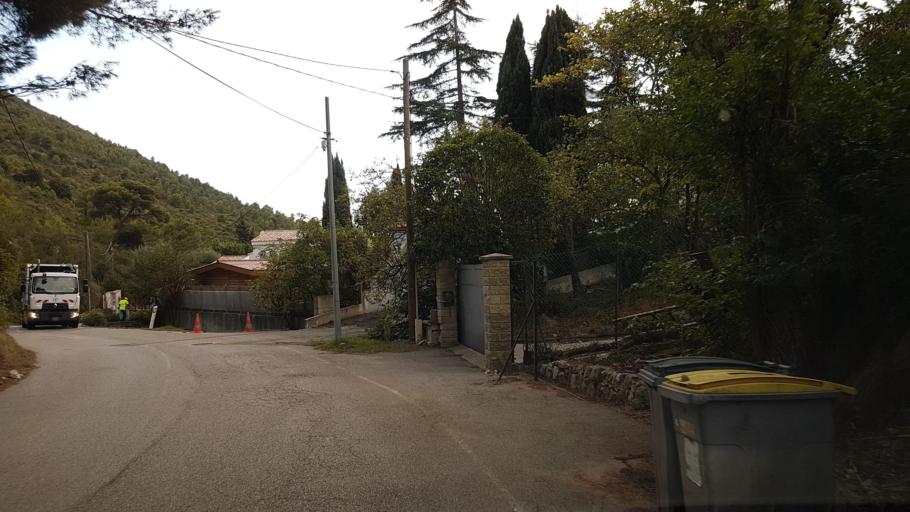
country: FR
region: Provence-Alpes-Cote d'Azur
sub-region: Departement des Alpes-Maritimes
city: La Turbie
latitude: 43.7363
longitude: 7.3938
